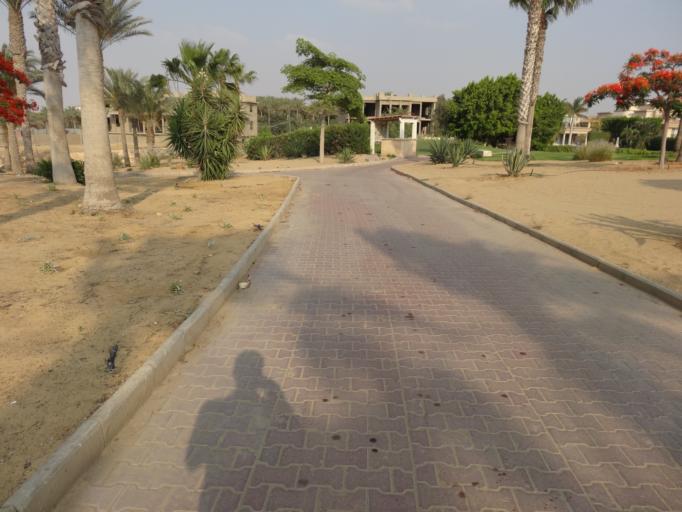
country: EG
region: Muhafazat al Qalyubiyah
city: Al Khankah
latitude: 30.0688
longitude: 31.4349
